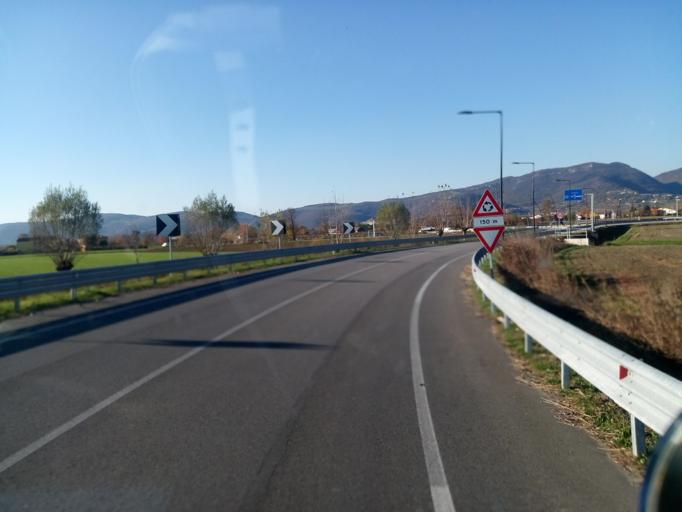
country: IT
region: Veneto
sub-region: Provincia di Vicenza
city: Ponte di Barbarano
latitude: 45.3849
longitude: 11.5671
